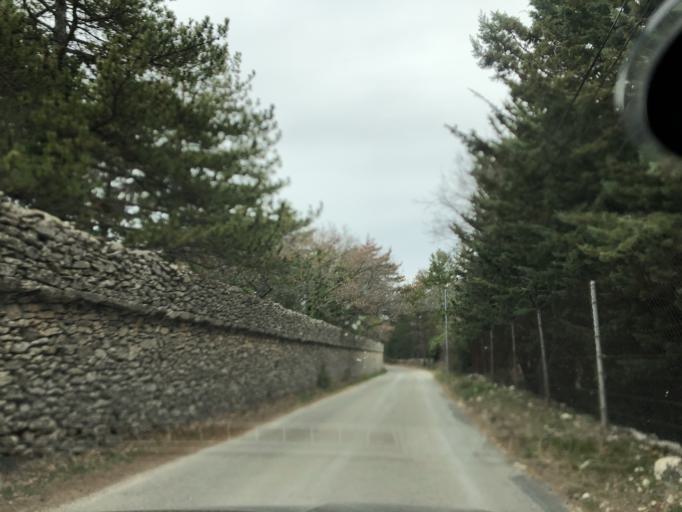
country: FR
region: Provence-Alpes-Cote d'Azur
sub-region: Departement du Vaucluse
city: Bonnieux
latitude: 43.8115
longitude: 5.3166
